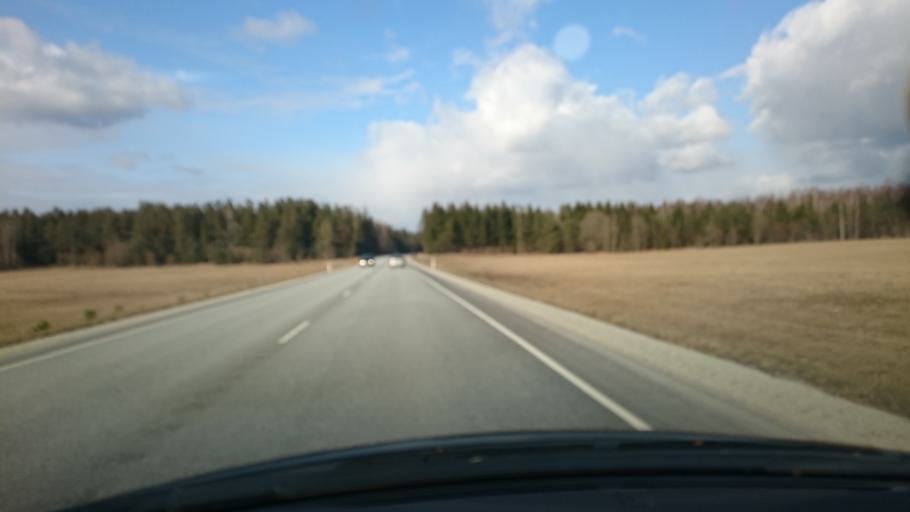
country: EE
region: Harju
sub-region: Nissi vald
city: Riisipere
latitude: 59.1889
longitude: 24.3985
